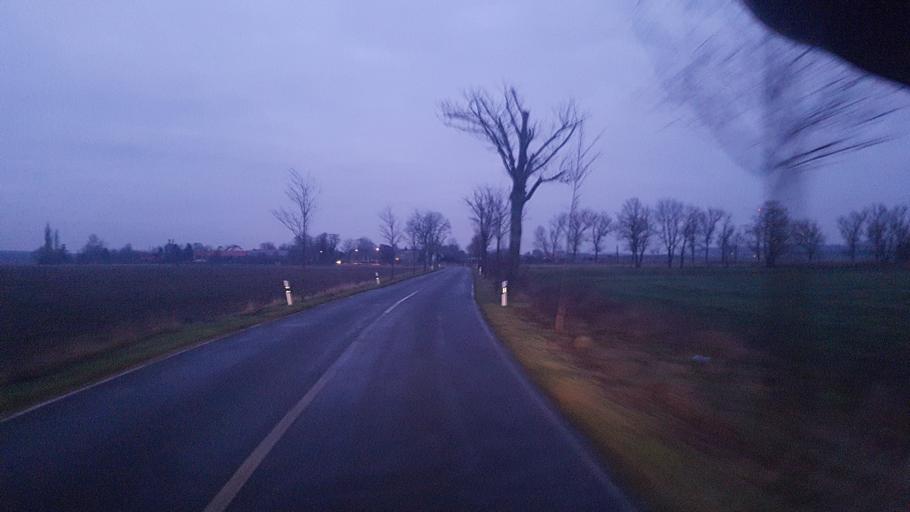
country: DE
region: Brandenburg
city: Luckenwalde
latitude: 52.1015
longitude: 13.1036
